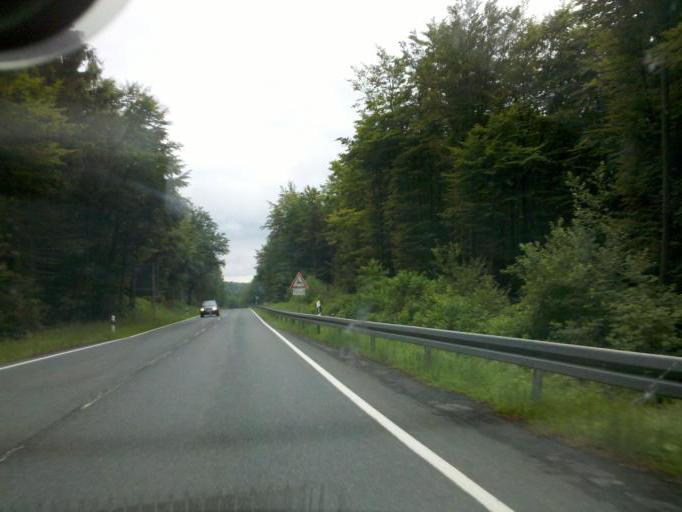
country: DE
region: North Rhine-Westphalia
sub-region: Regierungsbezirk Arnsberg
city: Wilnsdorf
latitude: 50.7956
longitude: 8.1451
